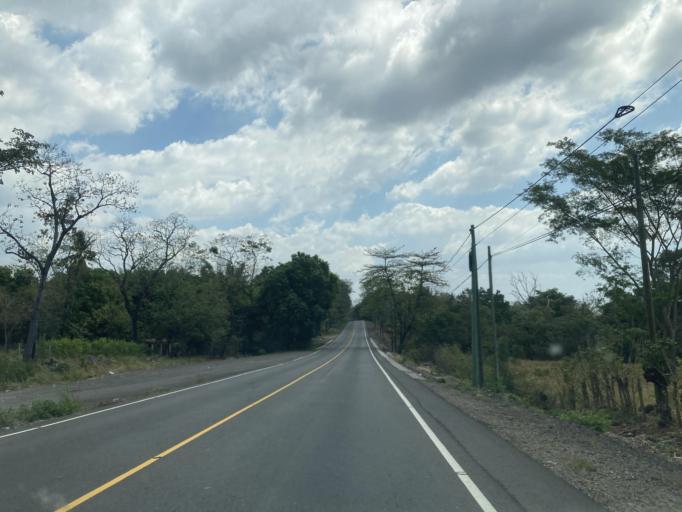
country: GT
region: Santa Rosa
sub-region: Municipio de Taxisco
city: Taxisco
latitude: 14.0897
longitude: -90.5076
